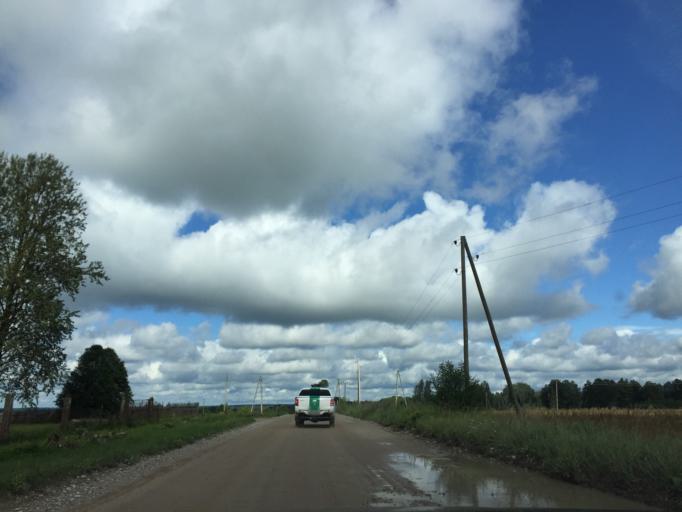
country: LV
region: Ligatne
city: Ligatne
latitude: 57.2073
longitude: 24.9613
